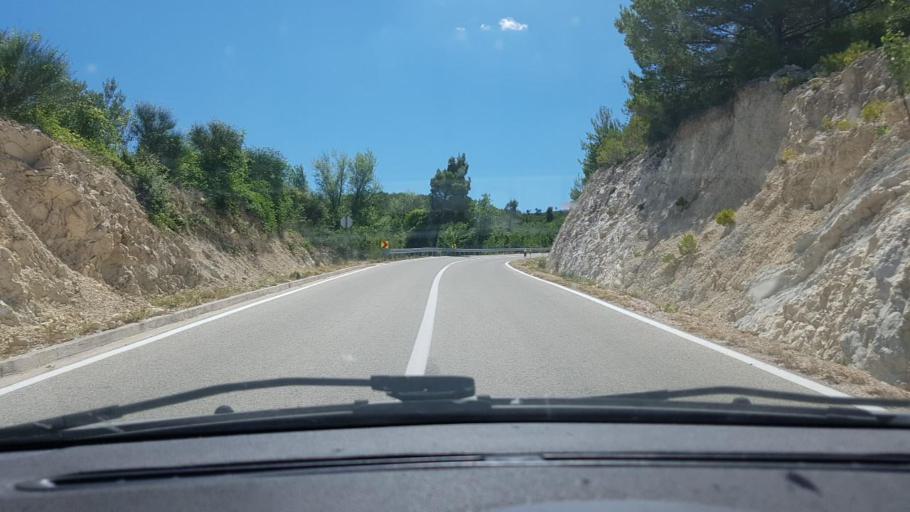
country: HR
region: Sibensko-Kniniska
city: Kistanje
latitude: 43.9056
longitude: 15.9128
